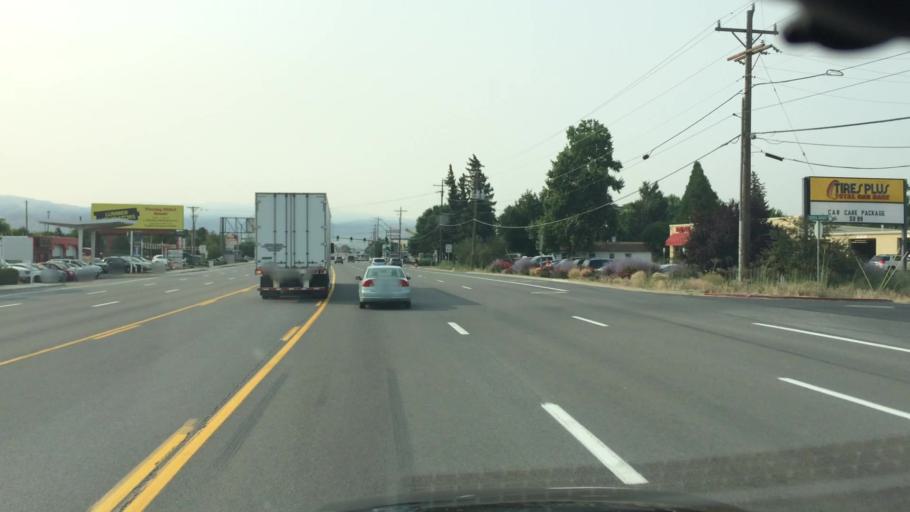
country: US
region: Nevada
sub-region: Washoe County
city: Sparks
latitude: 39.4436
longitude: -119.7728
